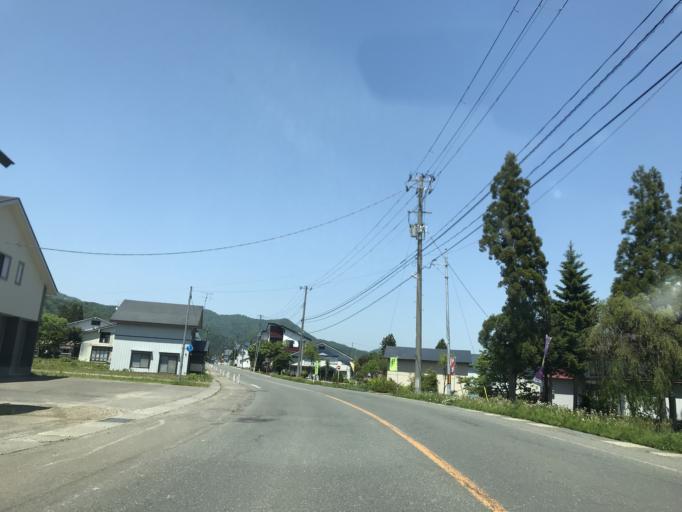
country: JP
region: Akita
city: Yokotemachi
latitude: 39.4284
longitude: 140.7503
